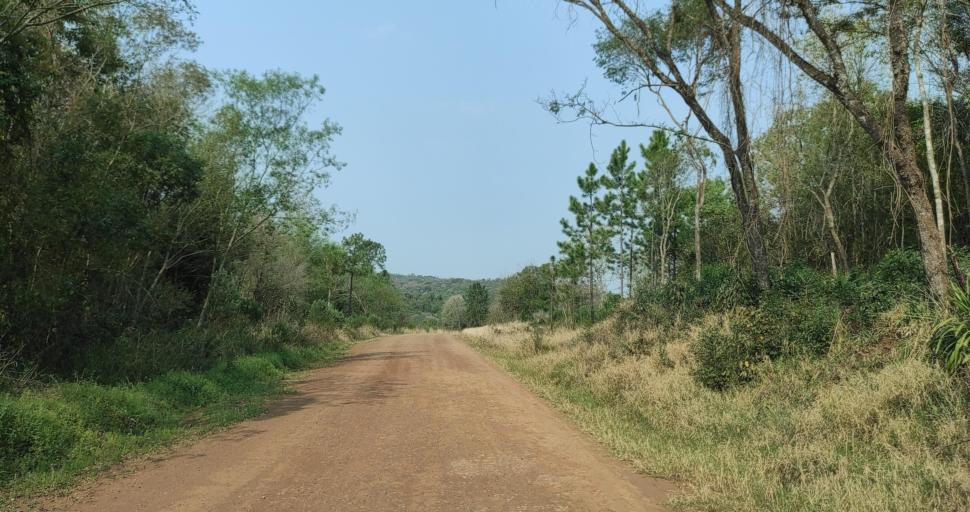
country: AR
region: Misiones
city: Cerro Cora
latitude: -27.5534
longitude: -55.5803
